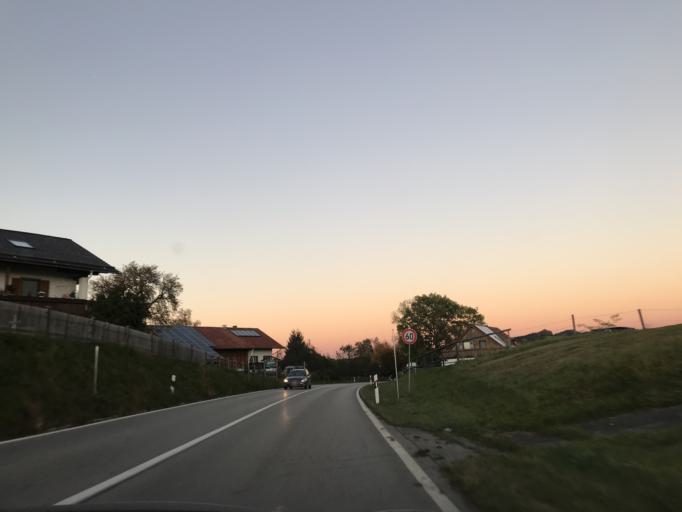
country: DE
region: Bavaria
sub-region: Upper Bavaria
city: Spatzenhausen
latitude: 47.7124
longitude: 11.2137
